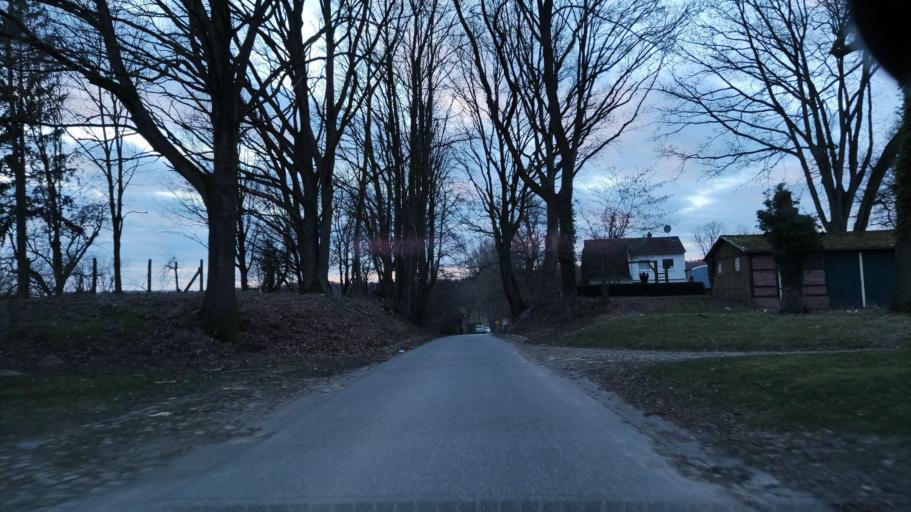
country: DE
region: Lower Saxony
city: Natendorf
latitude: 53.0728
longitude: 10.4446
